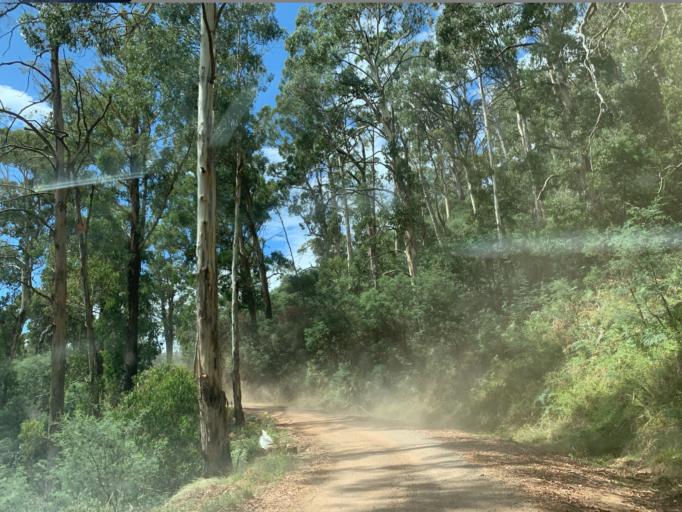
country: AU
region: Victoria
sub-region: Mansfield
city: Mansfield
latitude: -37.0931
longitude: 146.5325
